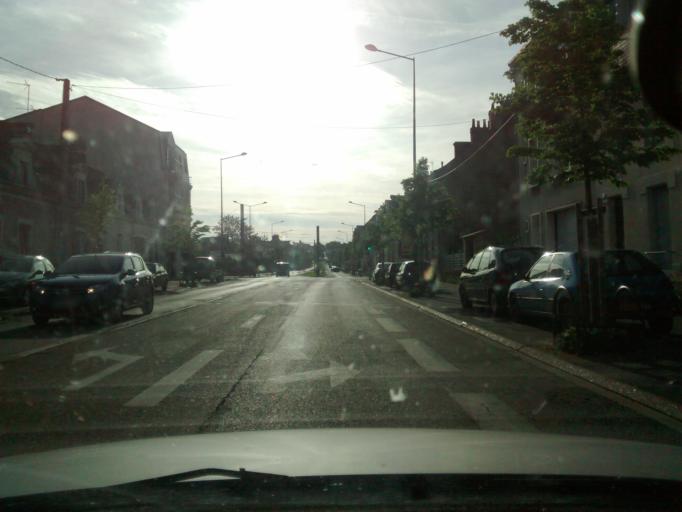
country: FR
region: Pays de la Loire
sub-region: Departement de la Sarthe
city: Le Mans
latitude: 48.0122
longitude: 0.1830
